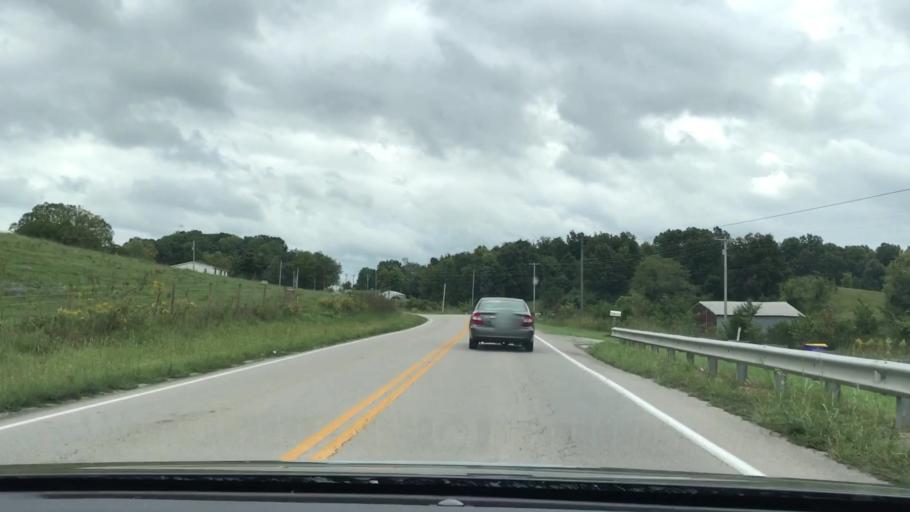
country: US
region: Kentucky
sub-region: Barren County
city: Glasgow
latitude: 36.9099
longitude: -85.7823
